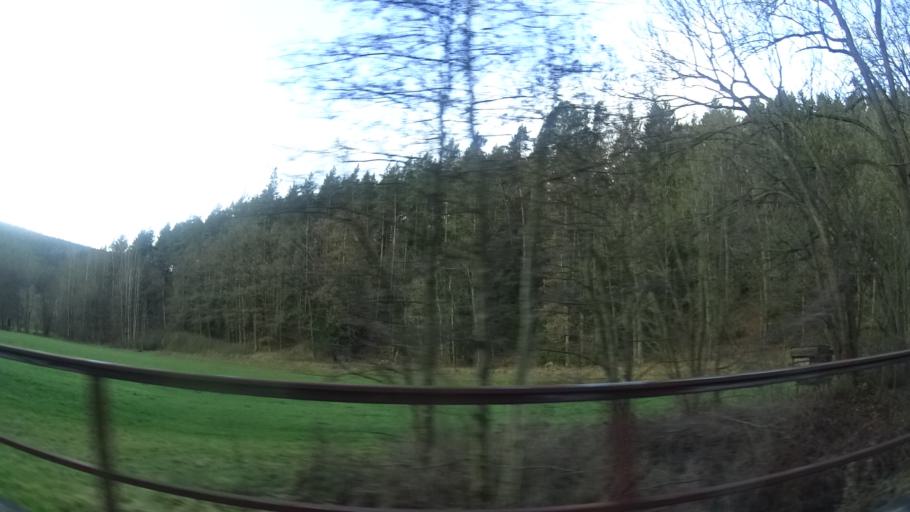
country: DE
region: Thuringia
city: Rottenbach
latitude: 50.7068
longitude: 11.1995
